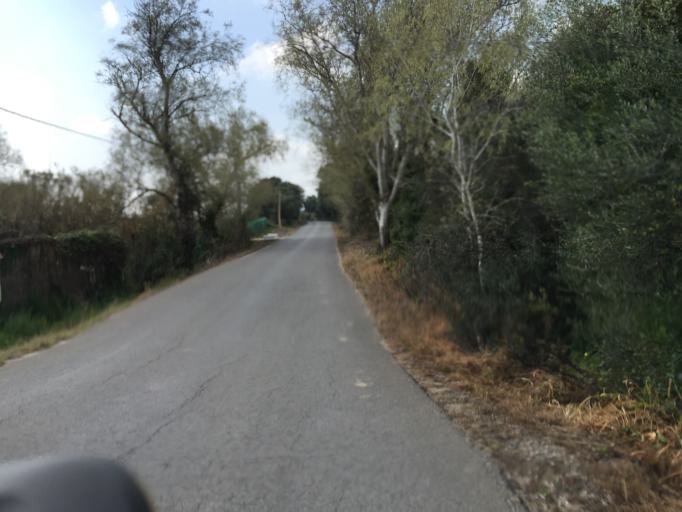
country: ES
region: Andalusia
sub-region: Provincia de Cadiz
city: Vejer de la Frontera
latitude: 36.2799
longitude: -5.9340
